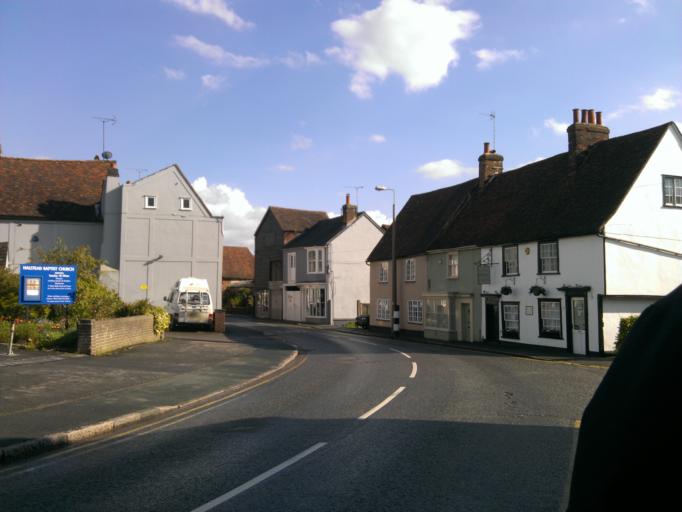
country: GB
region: England
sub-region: Essex
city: Sible Hedingham
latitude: 51.9460
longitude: 0.6381
